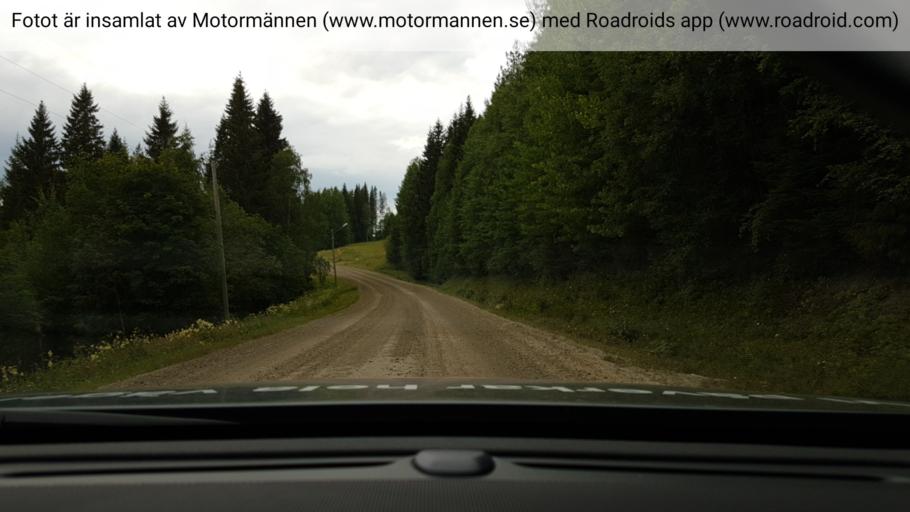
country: SE
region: Vaesterbotten
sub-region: Vannas Kommun
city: Vannasby
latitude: 64.0967
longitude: 20.0124
